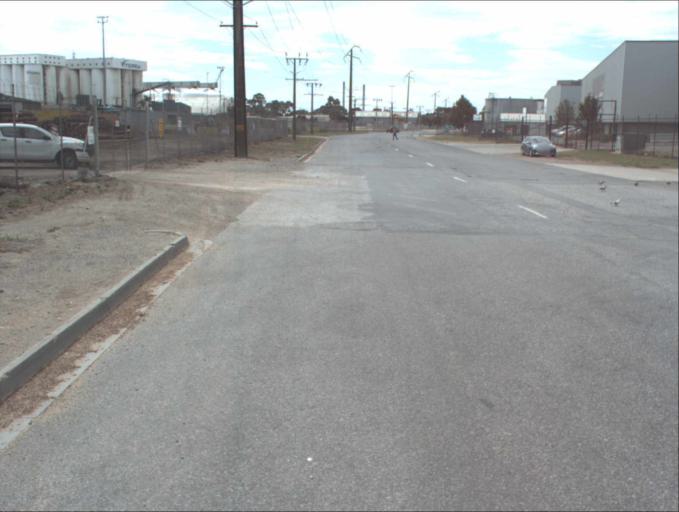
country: AU
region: South Australia
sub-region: Port Adelaide Enfield
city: Birkenhead
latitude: -34.8339
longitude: 138.5132
